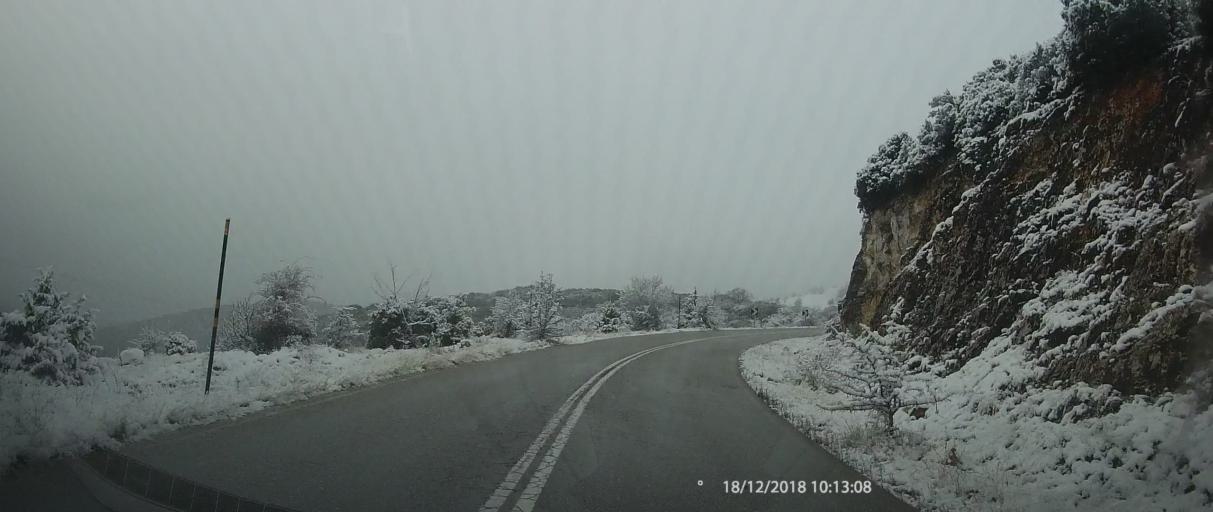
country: GR
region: Thessaly
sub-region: Nomos Larisis
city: Livadi
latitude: 40.1039
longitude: 22.2114
